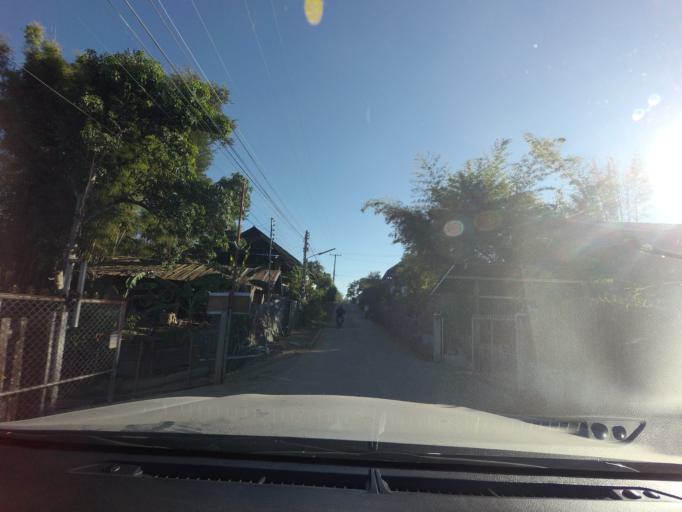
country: TH
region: Mae Hong Son
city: Wiang Nuea
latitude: 19.3970
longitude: 98.4217
